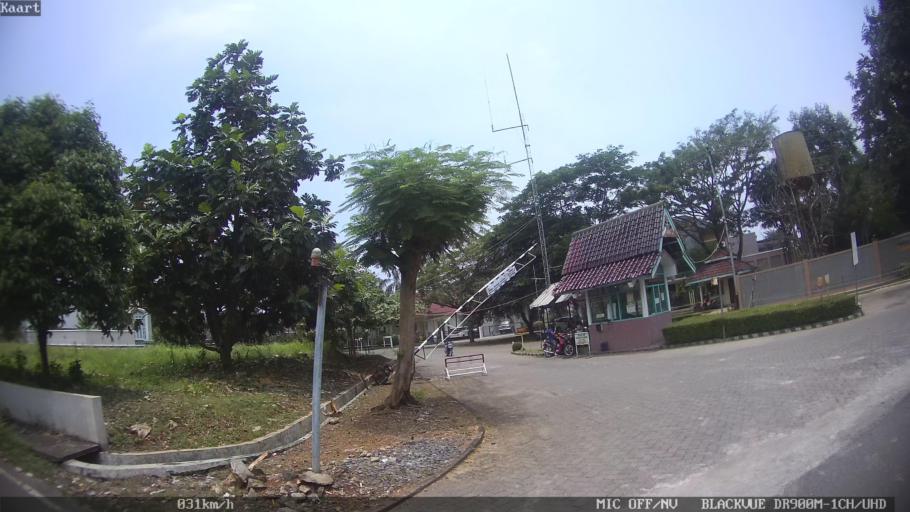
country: ID
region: Lampung
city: Bandarlampung
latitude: -5.4127
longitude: 105.2758
